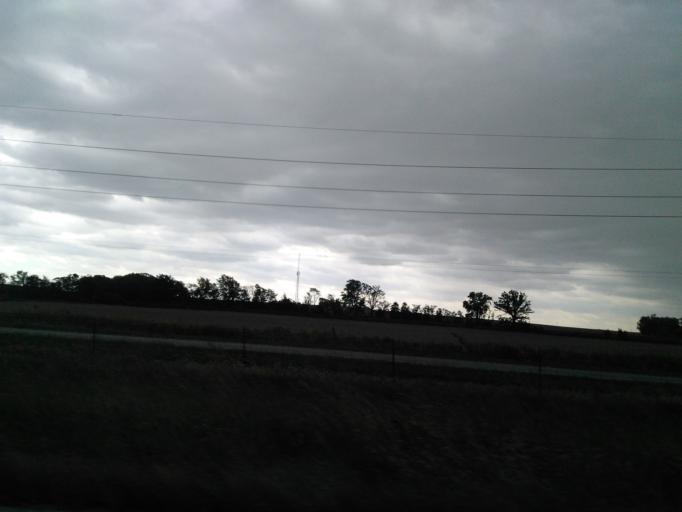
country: US
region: Illinois
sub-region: Bond County
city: Greenville
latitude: 38.8493
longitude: -89.4645
